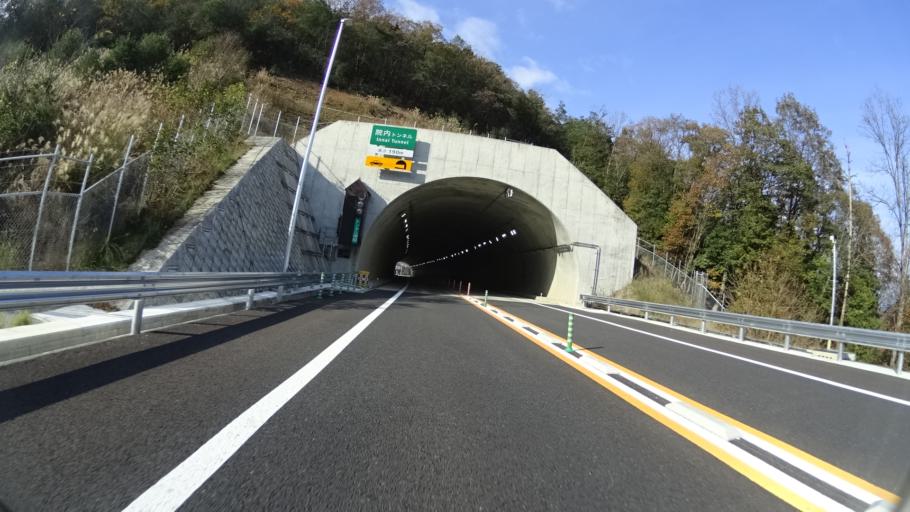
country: JP
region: Kyoto
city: Ayabe
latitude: 35.1603
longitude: 135.3993
